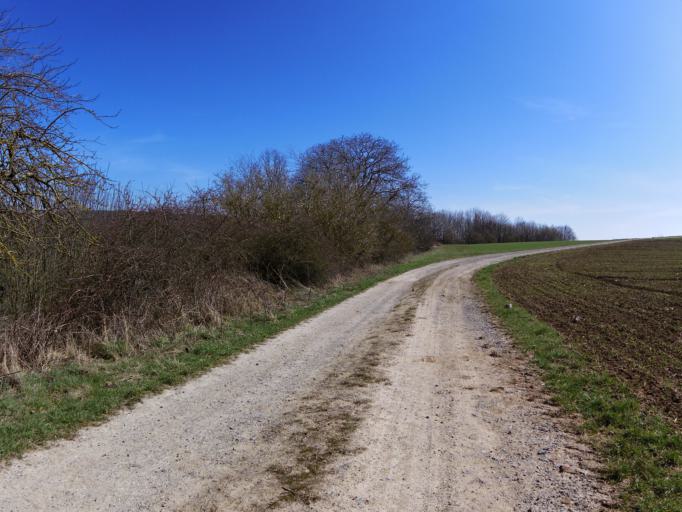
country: DE
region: Bavaria
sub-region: Regierungsbezirk Unterfranken
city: Prosselsheim
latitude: 49.8541
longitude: 10.1370
